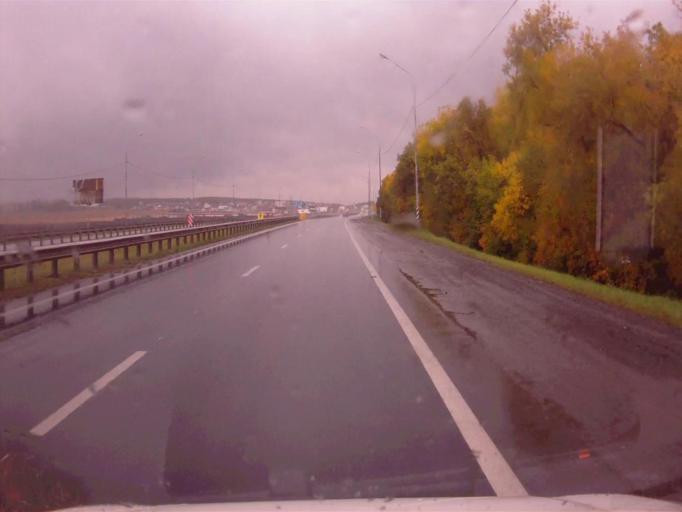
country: RU
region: Chelyabinsk
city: Dolgoderevenskoye
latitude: 55.2693
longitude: 61.3448
